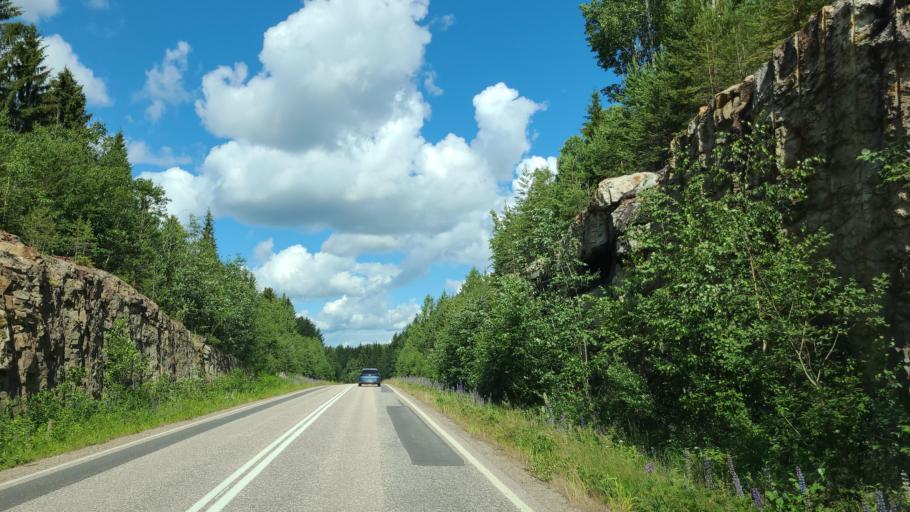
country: FI
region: Northern Savo
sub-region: Koillis-Savo
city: Kaavi
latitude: 62.9158
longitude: 28.7035
